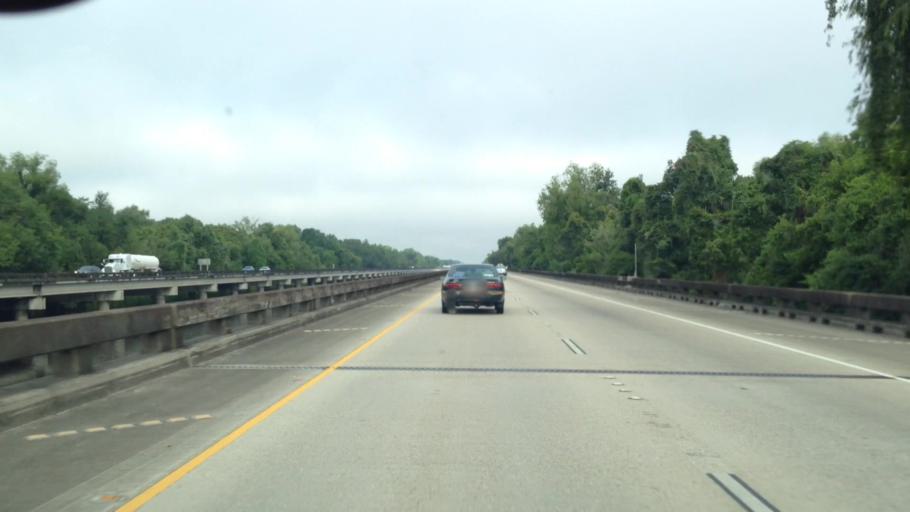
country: US
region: Louisiana
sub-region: Saint John the Baptist Parish
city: Montegut
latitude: 30.1097
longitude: -90.5279
